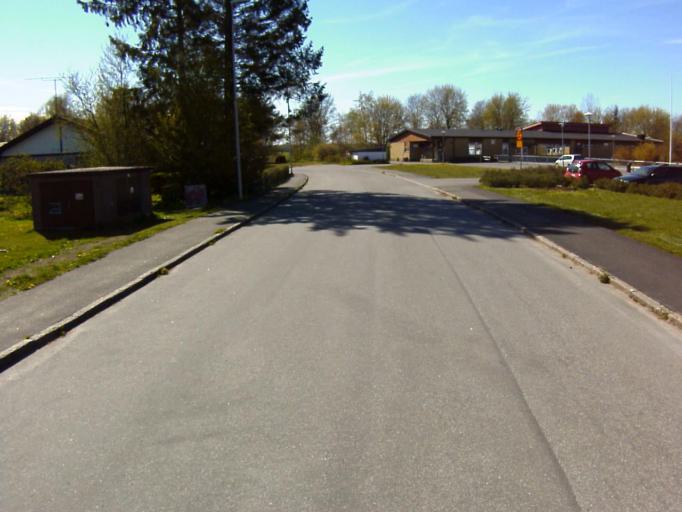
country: SE
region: Skane
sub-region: Kristianstads Kommun
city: Kristianstad
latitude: 56.0123
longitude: 14.1453
